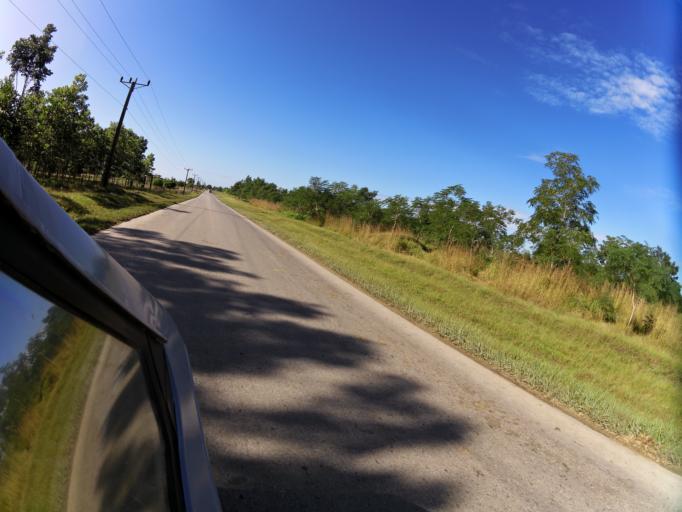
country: CU
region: Las Tunas
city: Las Tunas
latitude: 20.9785
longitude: -76.9032
